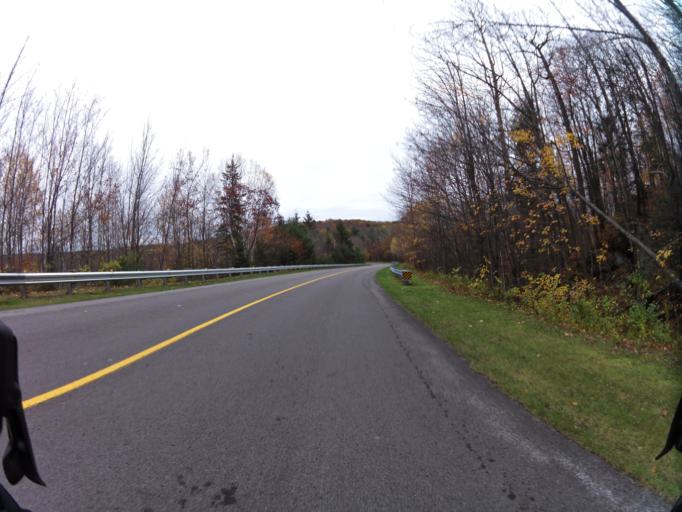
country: CA
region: Quebec
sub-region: Outaouais
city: Gatineau
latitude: 45.5030
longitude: -75.8271
